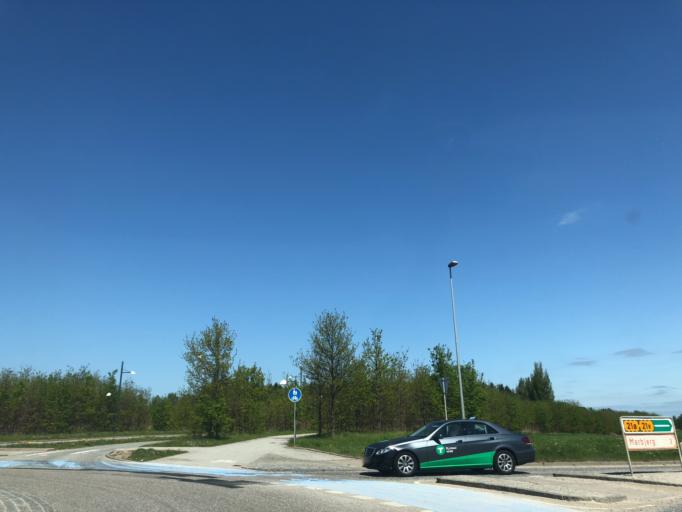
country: DK
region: Zealand
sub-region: Roskilde Kommune
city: Vindinge
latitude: 55.6504
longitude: 12.1444
